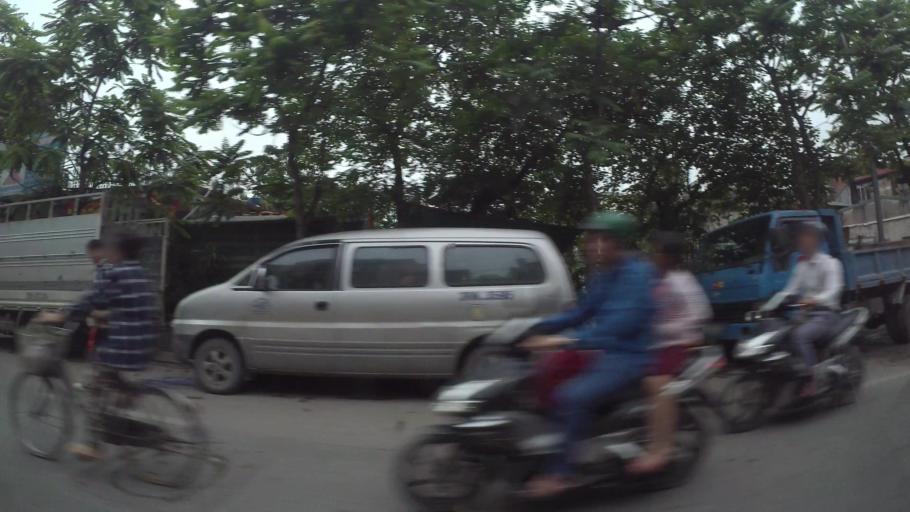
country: VN
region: Ha Noi
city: Hai BaTrung
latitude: 20.9956
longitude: 105.8740
